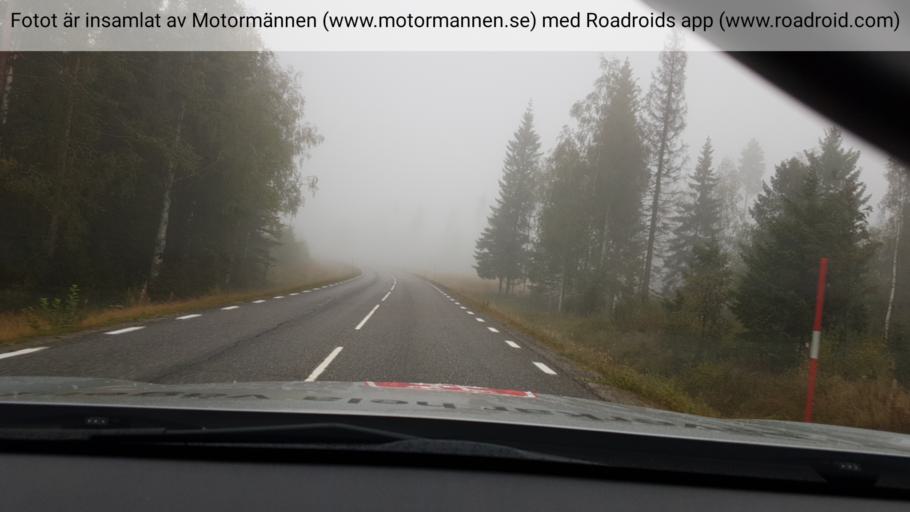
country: SE
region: Vaesterbotten
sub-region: Umea Kommun
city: Ersmark
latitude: 64.1111
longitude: 20.1711
